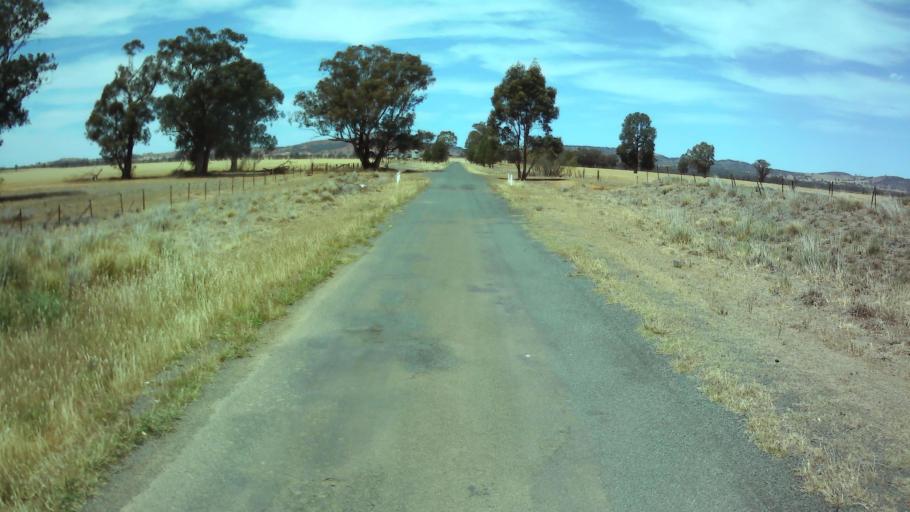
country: AU
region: New South Wales
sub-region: Weddin
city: Grenfell
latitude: -33.7565
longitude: 148.0914
